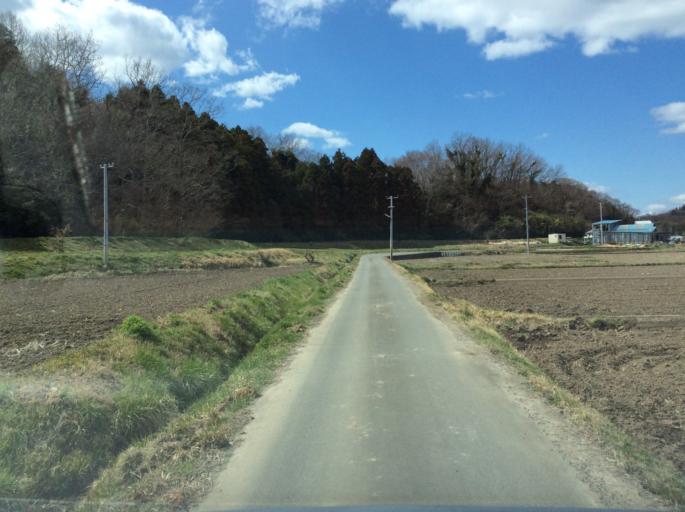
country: JP
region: Fukushima
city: Iwaki
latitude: 37.0855
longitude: 140.9484
